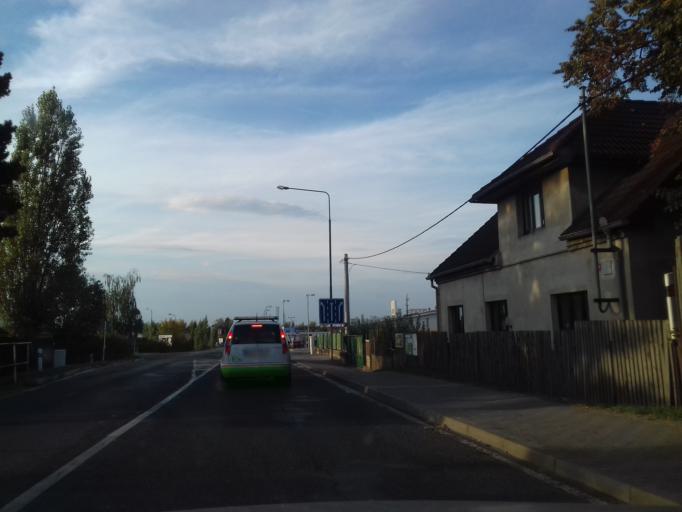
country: CZ
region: Central Bohemia
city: Vestec
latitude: 49.9815
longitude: 14.4970
